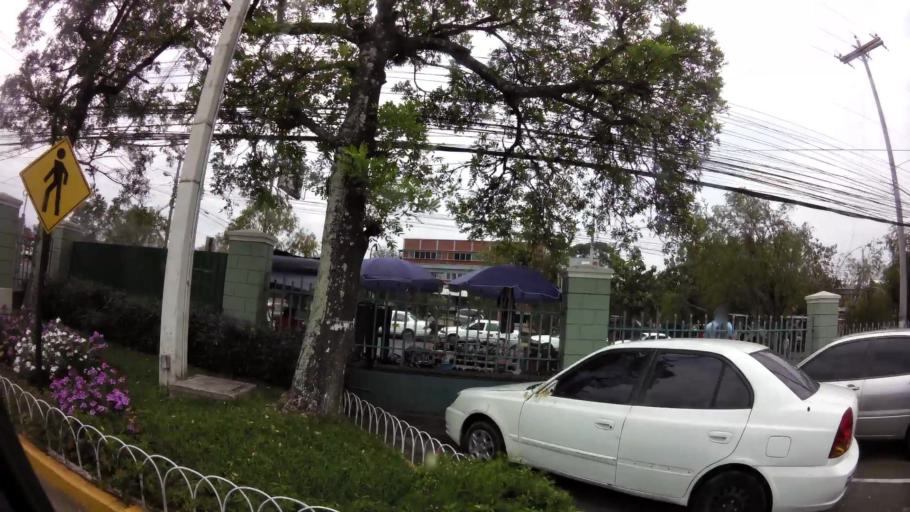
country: HN
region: Francisco Morazan
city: Tegucigalpa
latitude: 14.0765
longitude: -87.1855
